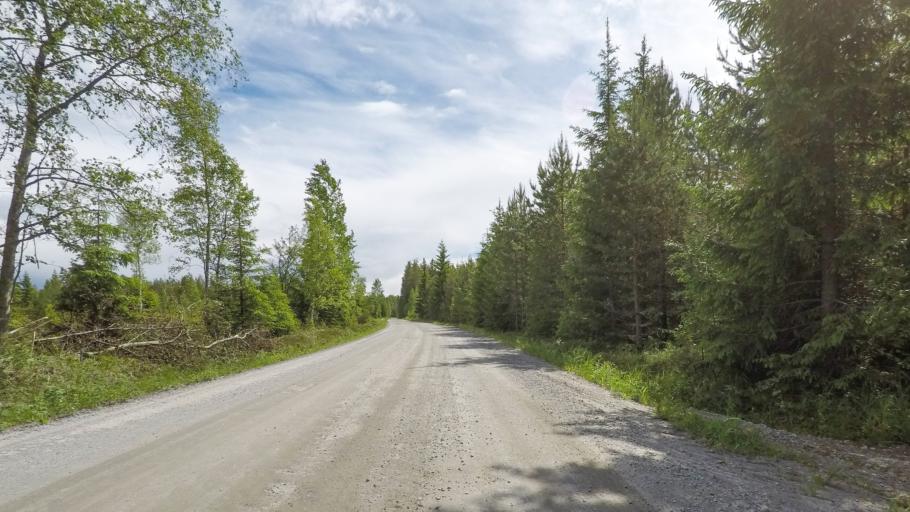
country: FI
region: Central Finland
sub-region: Jyvaeskylae
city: Hankasalmi
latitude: 62.3956
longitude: 26.5959
